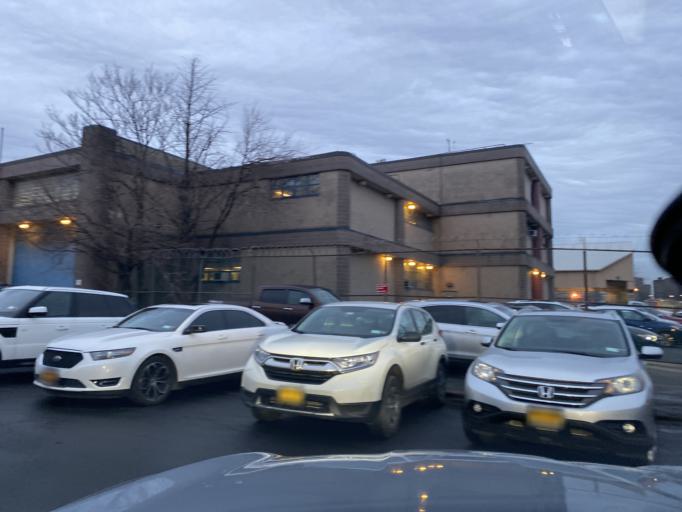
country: US
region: New York
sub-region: New York County
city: Inwood
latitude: 40.8684
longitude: -73.9122
